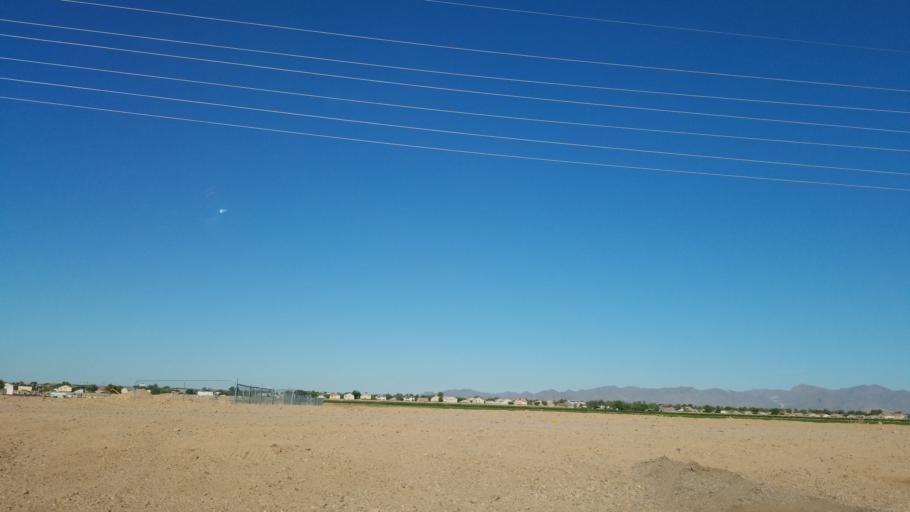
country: US
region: Arizona
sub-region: Maricopa County
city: Goodyear
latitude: 33.4433
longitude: -112.3755
